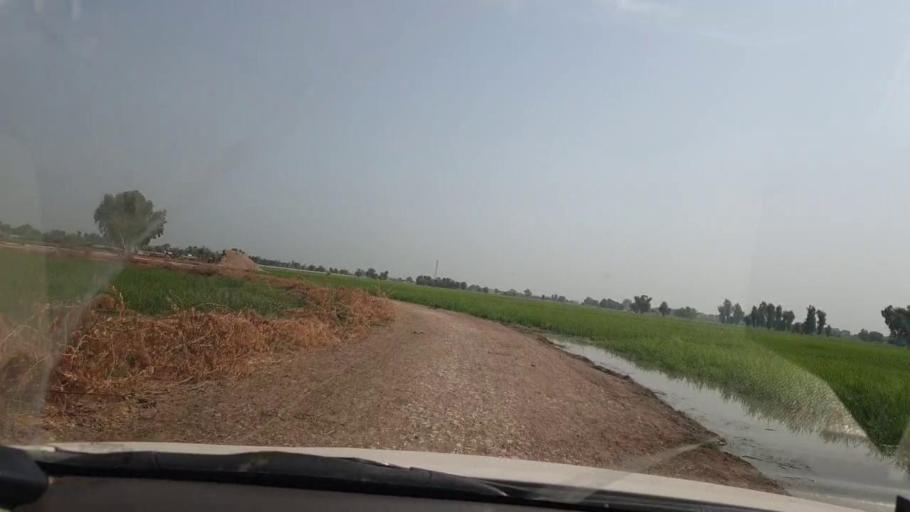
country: PK
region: Sindh
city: Chak
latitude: 27.8380
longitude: 68.7992
